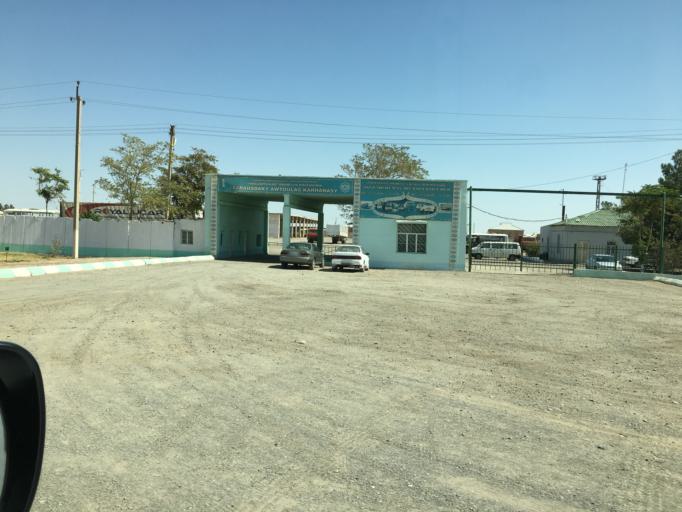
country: IR
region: Razavi Khorasan
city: Sarakhs
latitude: 36.5364
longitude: 61.2204
